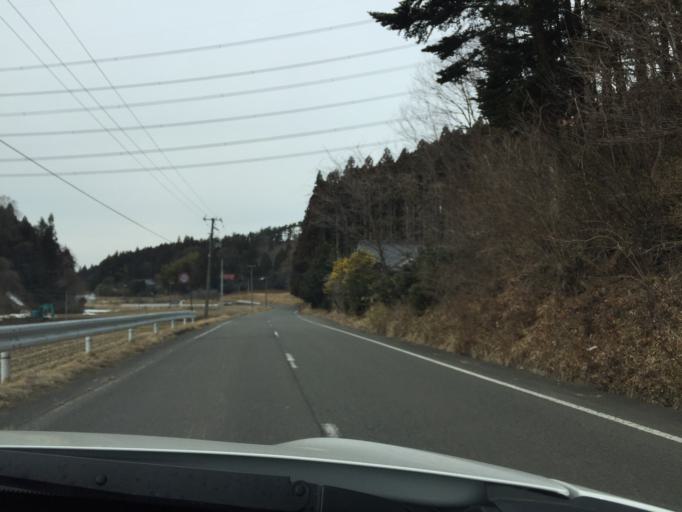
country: JP
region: Fukushima
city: Ishikawa
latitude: 37.1773
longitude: 140.5950
